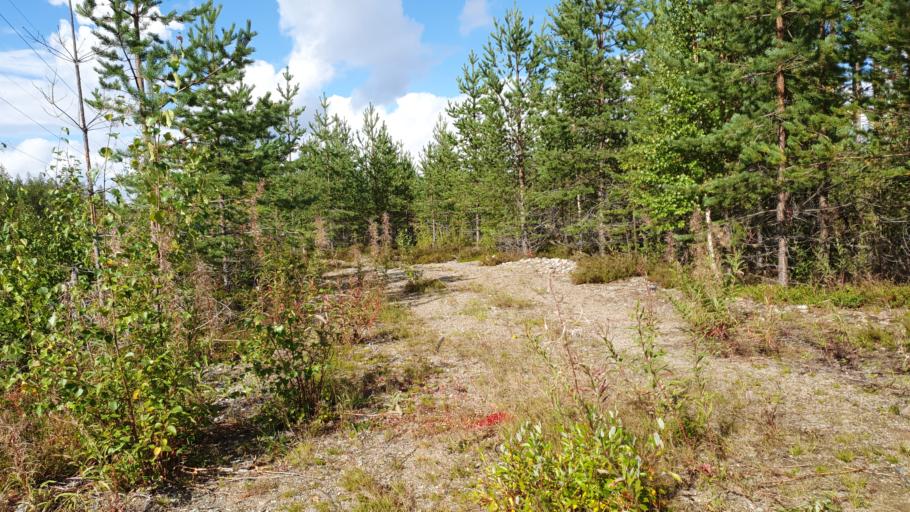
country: FI
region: Kainuu
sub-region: Kehys-Kainuu
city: Kuhmo
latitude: 64.1330
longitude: 29.3830
